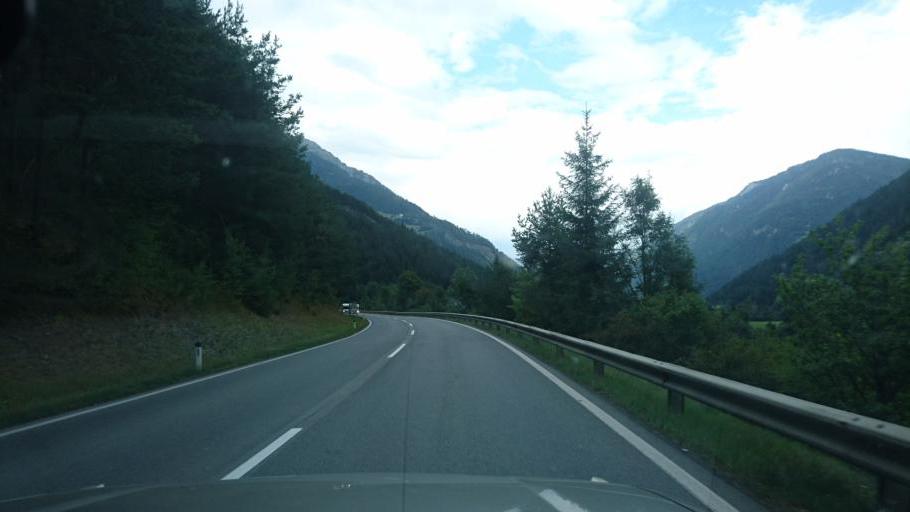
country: AT
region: Tyrol
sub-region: Politischer Bezirk Landeck
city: Pfunds
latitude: 46.9549
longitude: 10.5122
